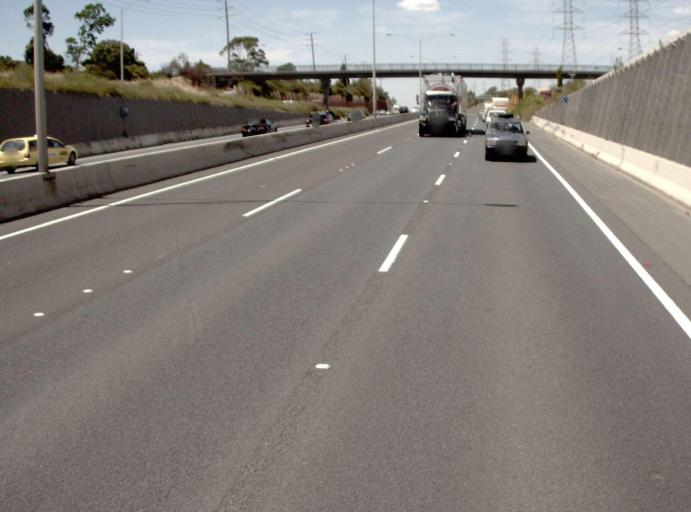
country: AU
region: Victoria
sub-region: Hume
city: Campbellfield
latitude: -37.6920
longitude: 144.9594
